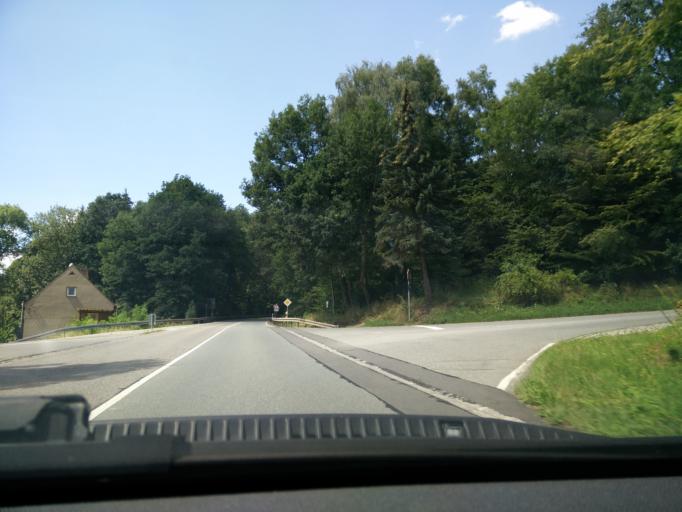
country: DE
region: Saxony
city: Penig
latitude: 50.9330
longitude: 12.6864
